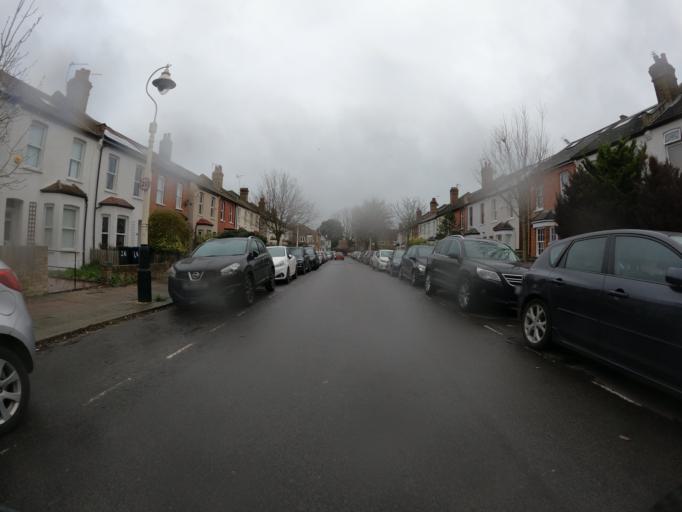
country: GB
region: England
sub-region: Greater London
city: Brentford
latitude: 51.5012
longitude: -0.3171
